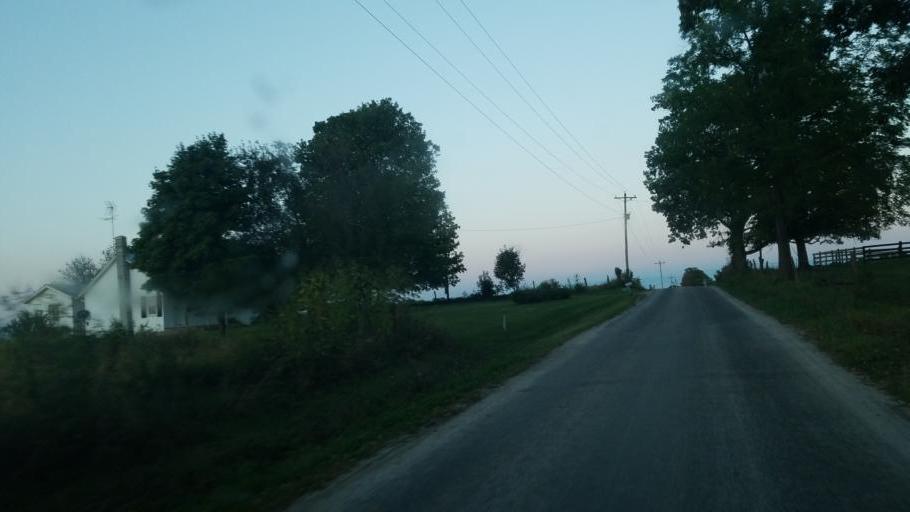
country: US
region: Ohio
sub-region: Ashland County
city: Ashland
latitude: 40.9313
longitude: -82.3984
